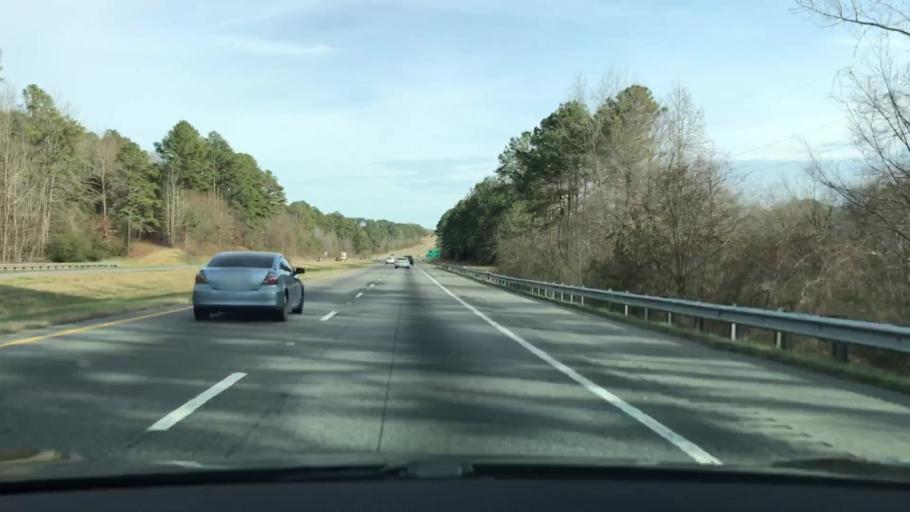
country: US
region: Georgia
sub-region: Walton County
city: Social Circle
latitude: 33.6112
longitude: -83.7166
